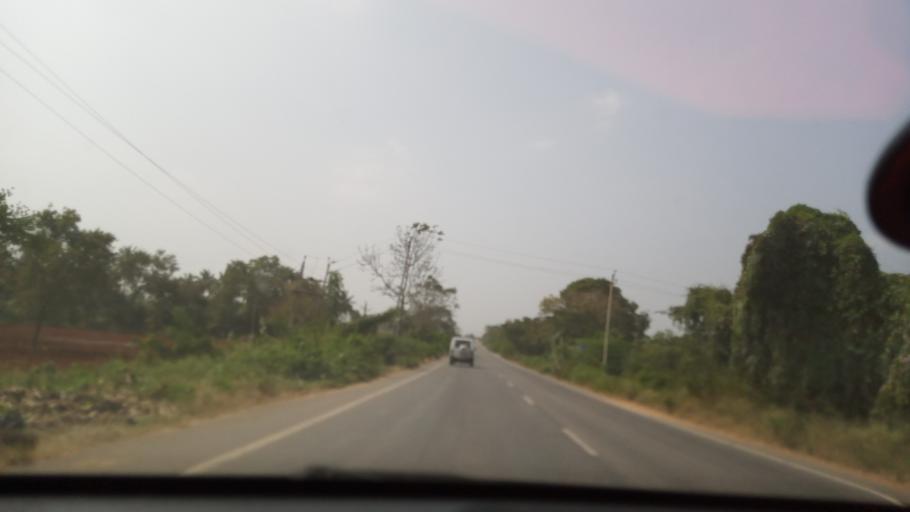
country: IN
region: Karnataka
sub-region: Chamrajnagar
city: Chamrajnagar
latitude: 11.9949
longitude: 76.8563
